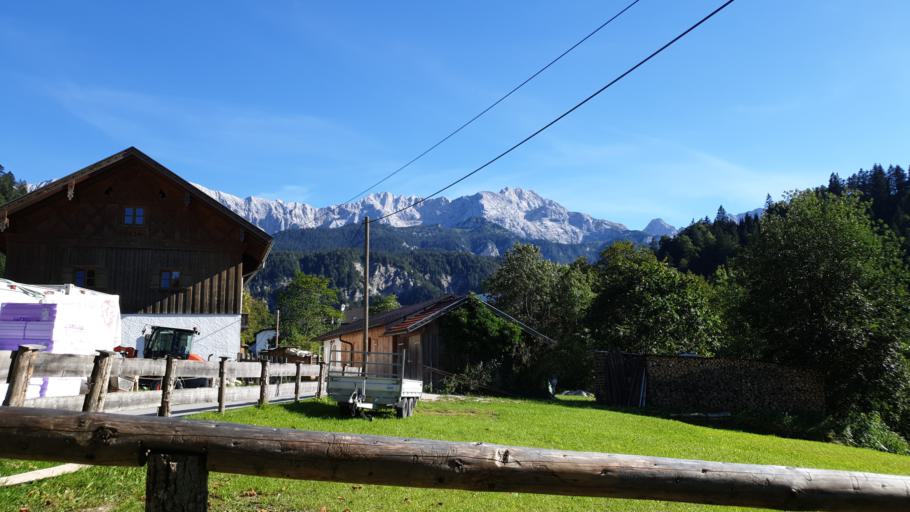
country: DE
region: Bavaria
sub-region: Upper Bavaria
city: Garmisch-Partenkirchen
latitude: 47.4681
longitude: 11.1217
